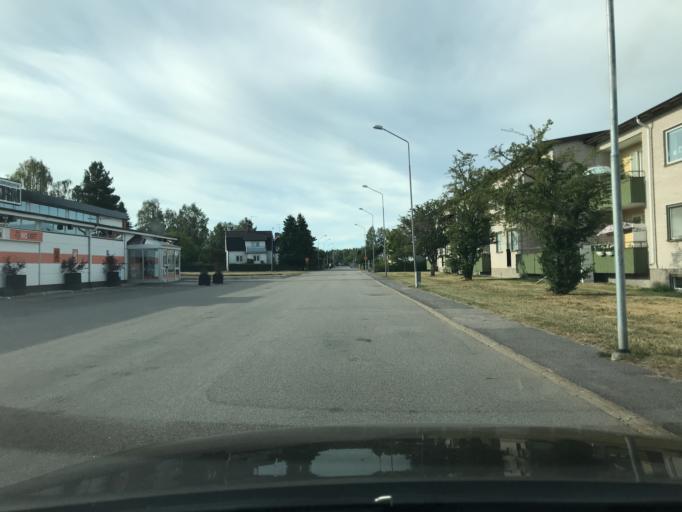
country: SE
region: Kalmar
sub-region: Hultsfreds Kommun
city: Hultsfred
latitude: 57.4951
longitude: 15.8436
